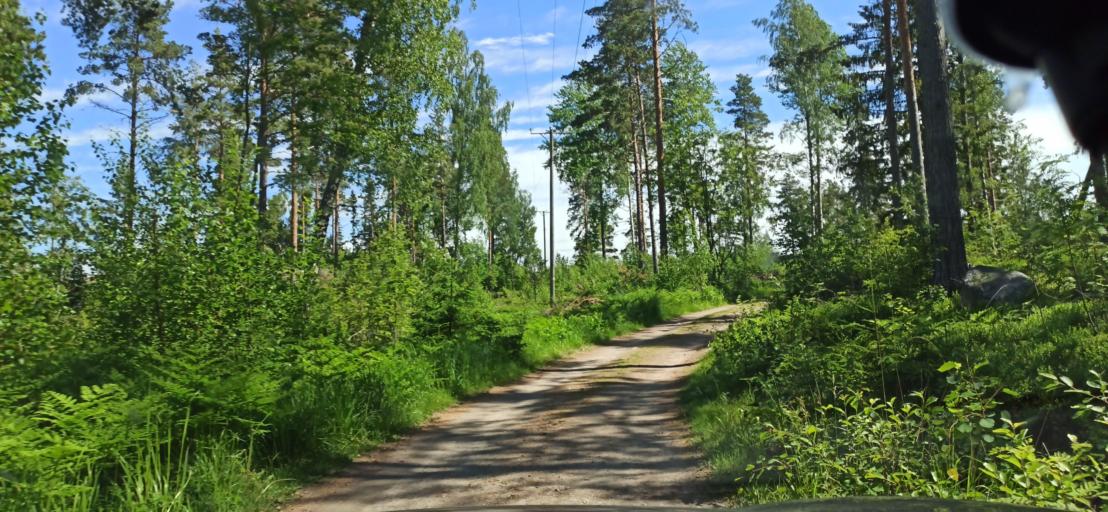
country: FI
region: Varsinais-Suomi
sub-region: Turku
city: Sauvo
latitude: 60.3823
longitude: 22.6221
